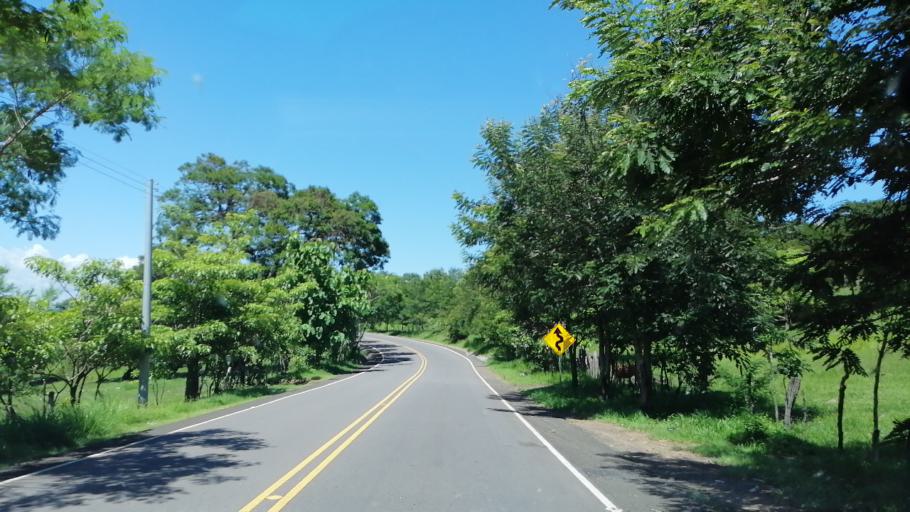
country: SV
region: Morazan
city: Cacaopera
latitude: 13.8091
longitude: -88.1564
